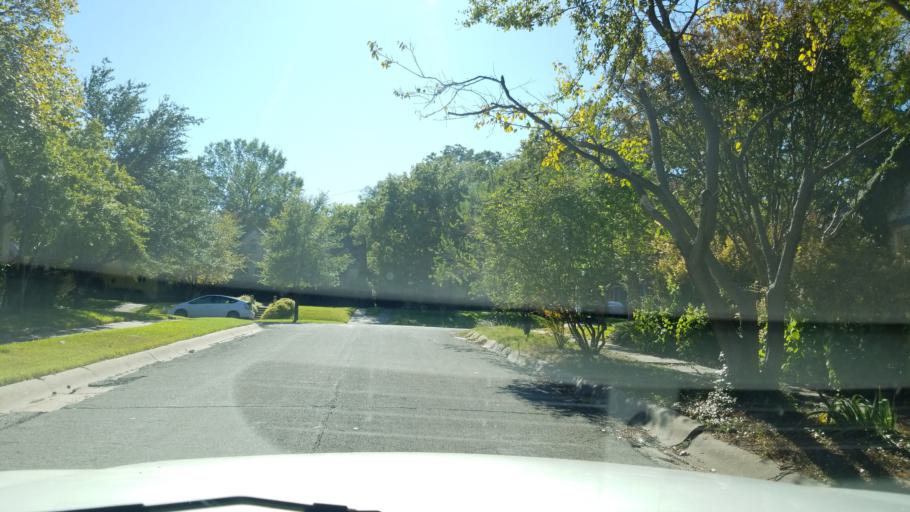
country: US
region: Texas
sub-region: Dallas County
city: Highland Park
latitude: 32.8078
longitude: -96.7430
